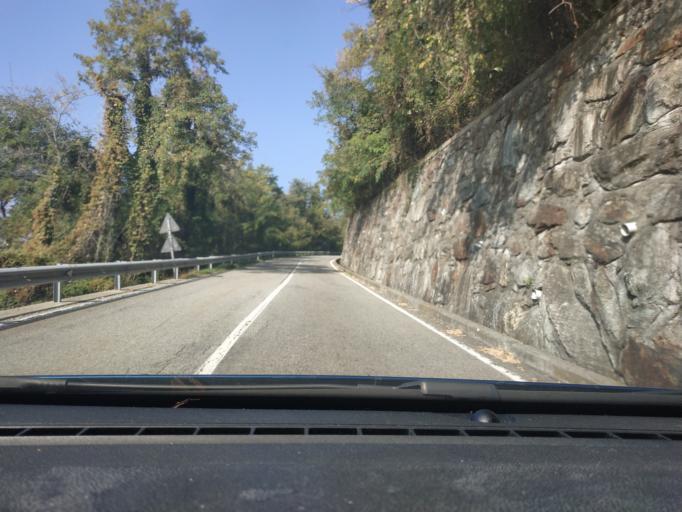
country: IT
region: Piedmont
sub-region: Provincia di Torino
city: Chiaverano
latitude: 45.5117
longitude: 7.9035
